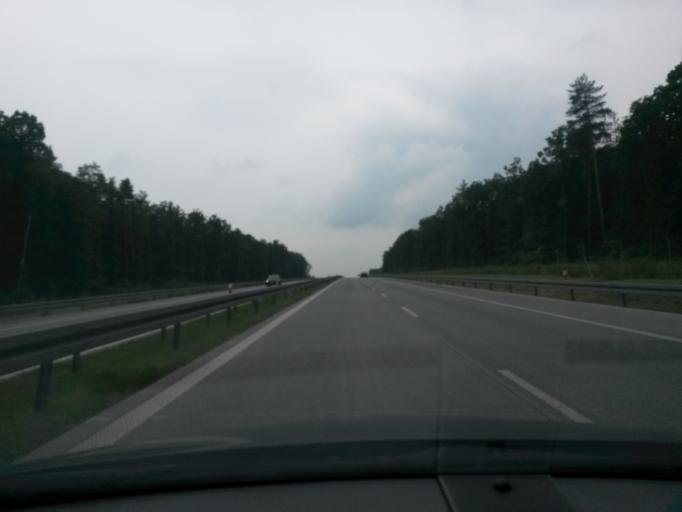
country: PL
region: Lodz Voivodeship
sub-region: Powiat rawski
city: Rawa Mazowiecka
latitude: 51.7257
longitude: 20.2259
